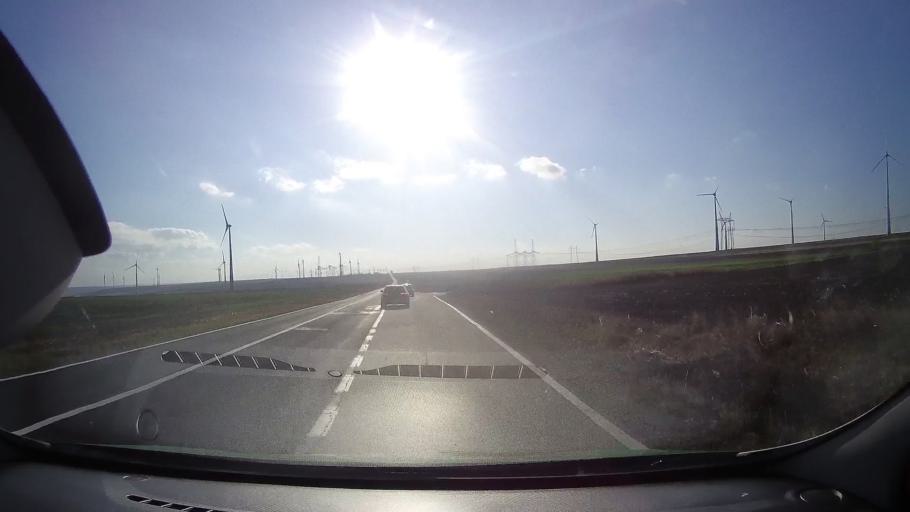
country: RO
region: Tulcea
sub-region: Comuna Topolog
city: Topolog
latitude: 44.8138
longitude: 28.2559
